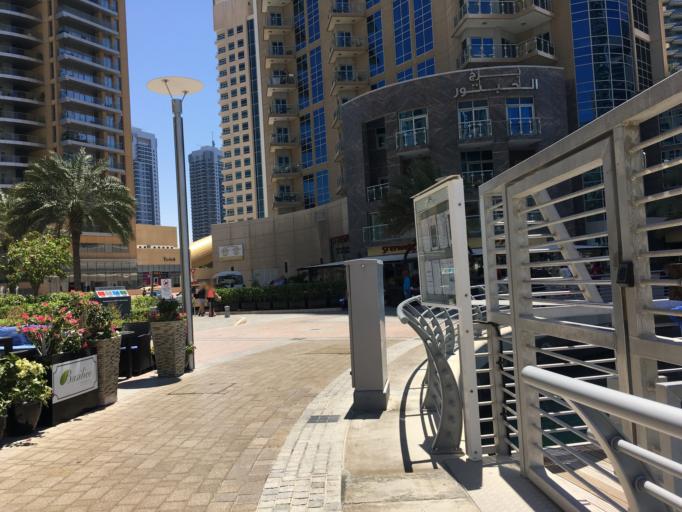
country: AE
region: Dubai
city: Dubai
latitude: 25.0838
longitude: 55.1478
